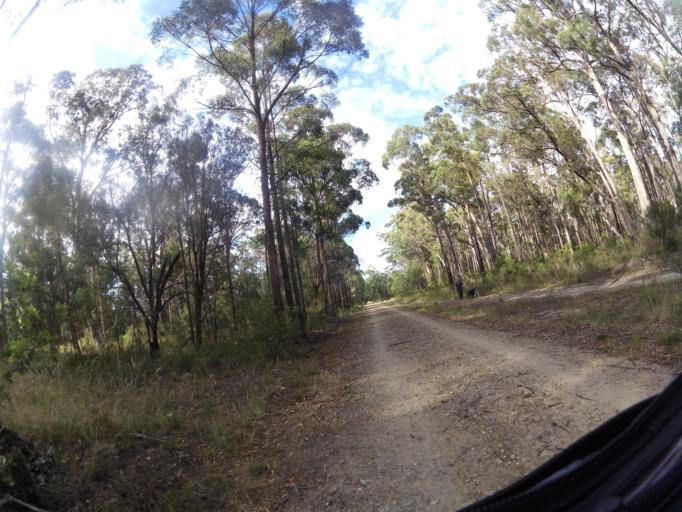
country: AU
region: Victoria
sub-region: East Gippsland
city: Lakes Entrance
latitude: -37.7395
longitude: 148.4193
